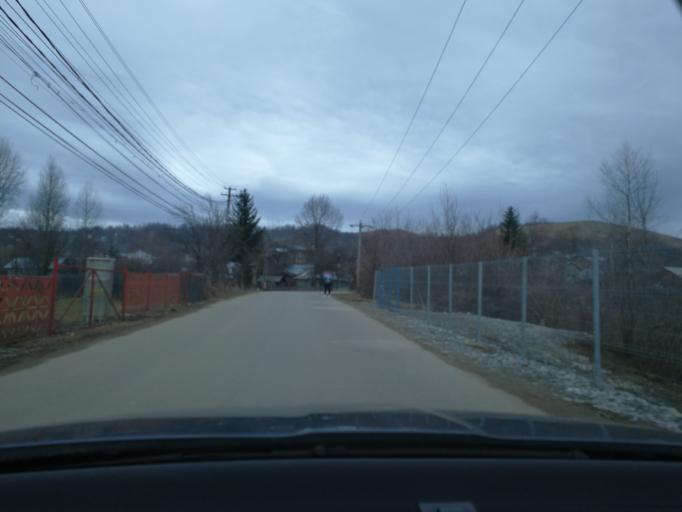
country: RO
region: Prahova
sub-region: Oras Breaza
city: Valea Tarsei
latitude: 45.1825
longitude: 25.6324
